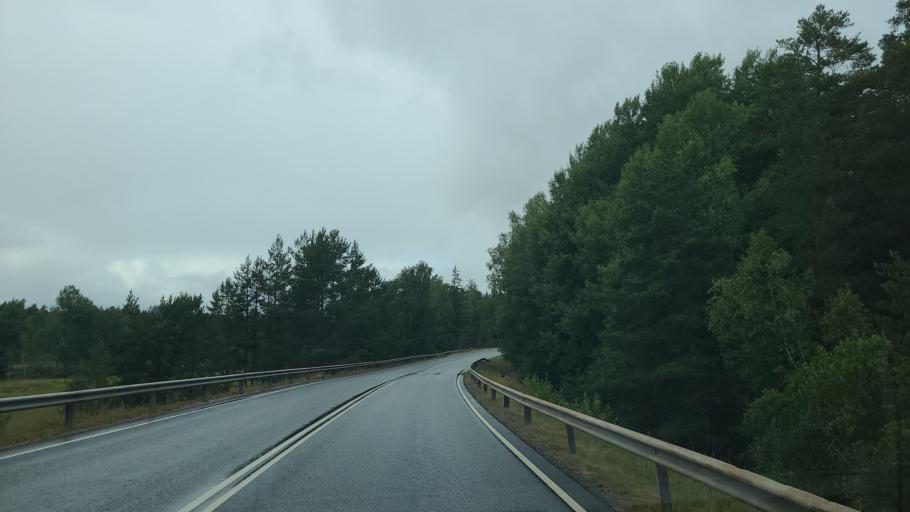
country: FI
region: Varsinais-Suomi
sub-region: Aboland-Turunmaa
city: Kimito
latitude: 60.2324
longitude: 22.6059
